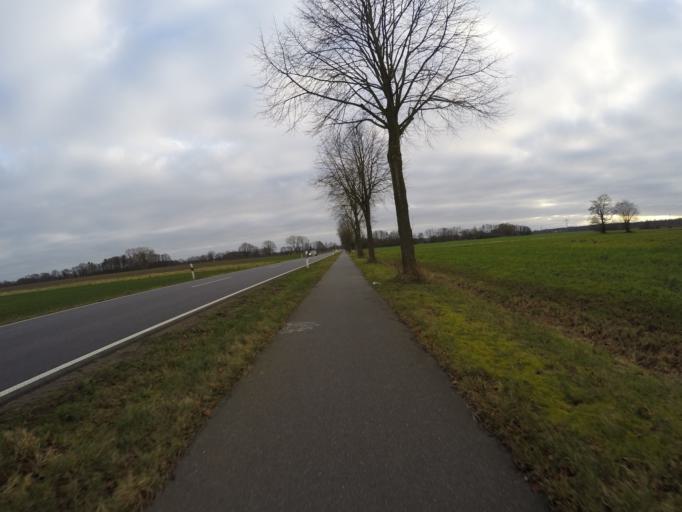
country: DE
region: Schleswig-Holstein
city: Alveslohe
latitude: 53.7694
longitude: 9.9066
